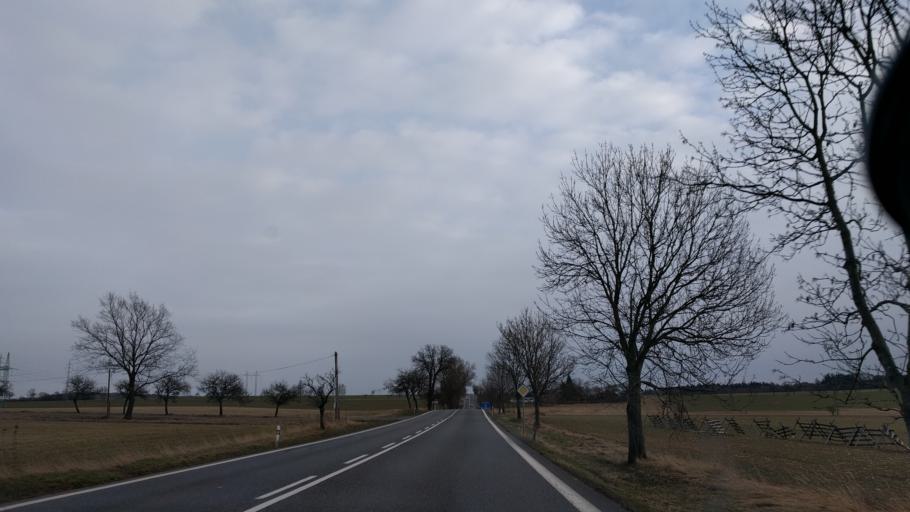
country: CZ
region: Central Bohemia
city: Milin
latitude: 49.6090
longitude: 14.0594
